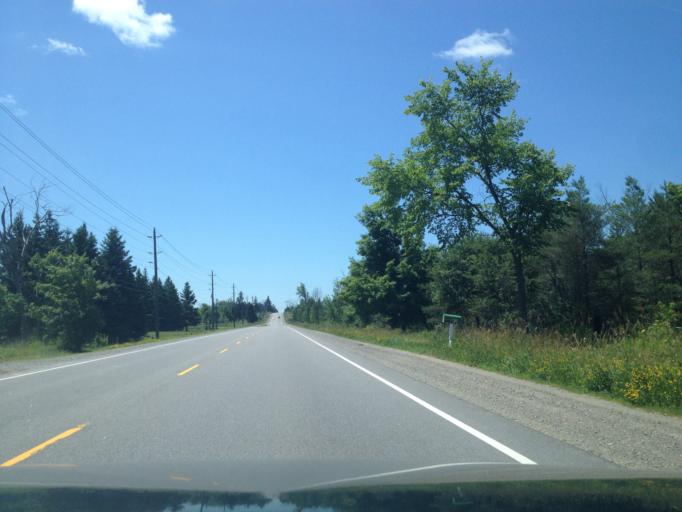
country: CA
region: Ontario
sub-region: Wellington County
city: Guelph
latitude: 43.6250
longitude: -80.0900
